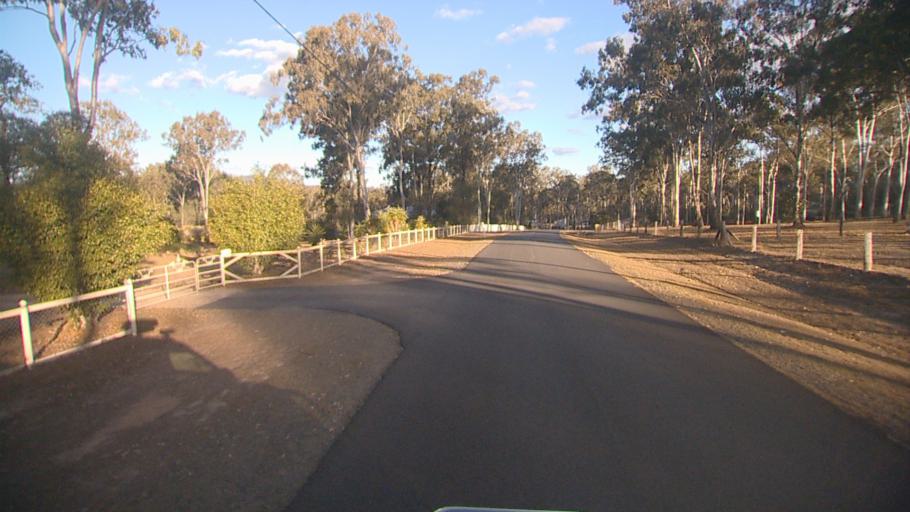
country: AU
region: Queensland
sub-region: Logan
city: Cedar Vale
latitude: -27.8559
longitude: 153.0979
